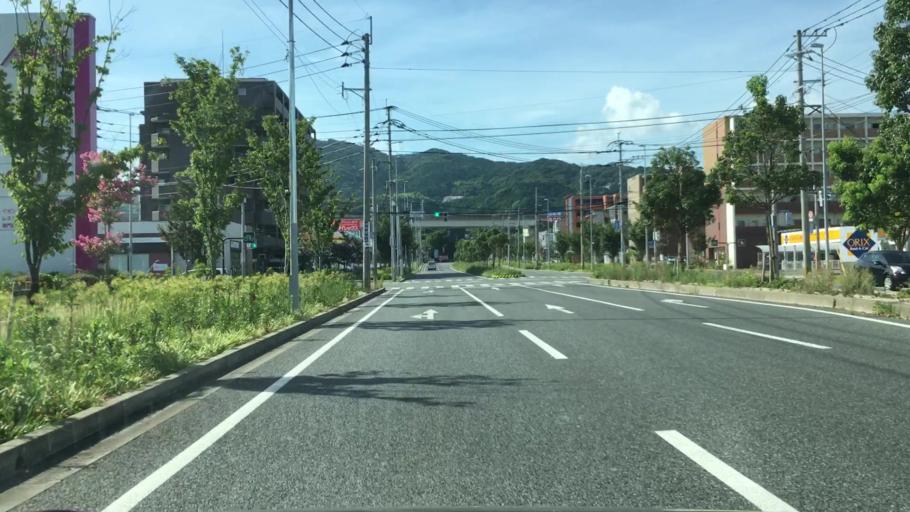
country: JP
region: Fukuoka
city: Maebaru-chuo
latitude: 33.5763
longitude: 130.2561
